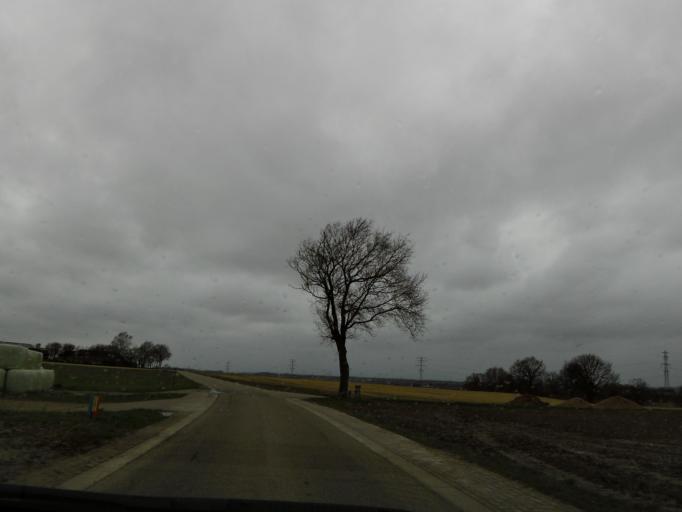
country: NL
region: Limburg
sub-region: Gemeente Voerendaal
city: Ubachsberg
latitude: 50.8531
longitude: 5.9261
